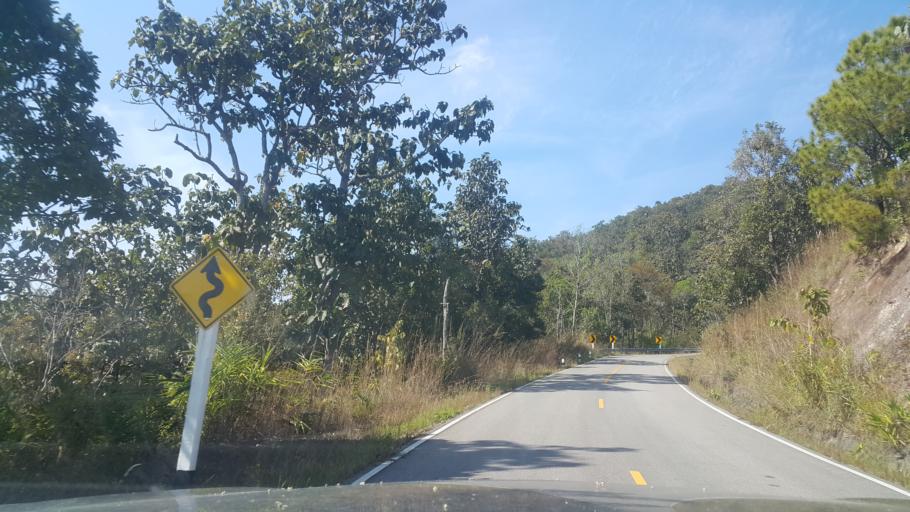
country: TH
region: Chiang Mai
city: Samoeng
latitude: 18.8994
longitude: 98.6766
